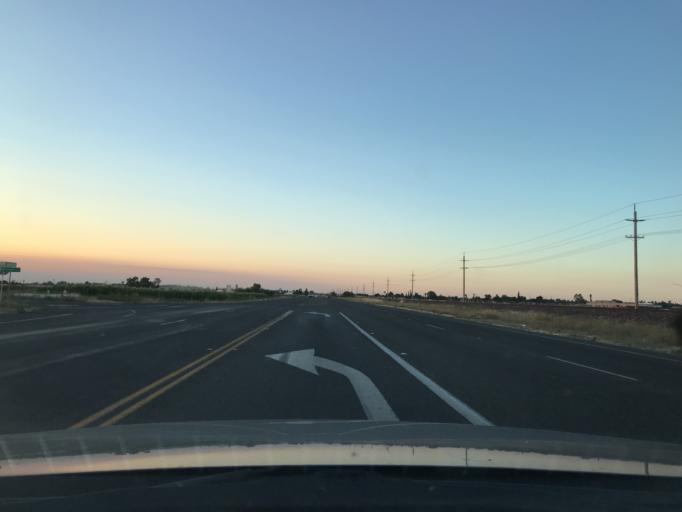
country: US
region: California
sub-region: Merced County
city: Merced
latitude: 37.3390
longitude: -120.5384
